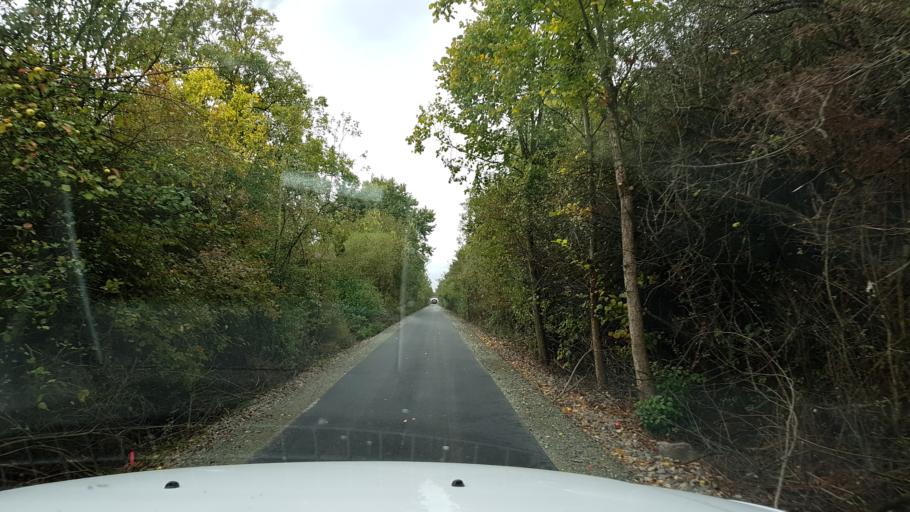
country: PL
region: West Pomeranian Voivodeship
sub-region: Powiat gryfinski
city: Moryn
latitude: 52.8686
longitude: 14.3682
